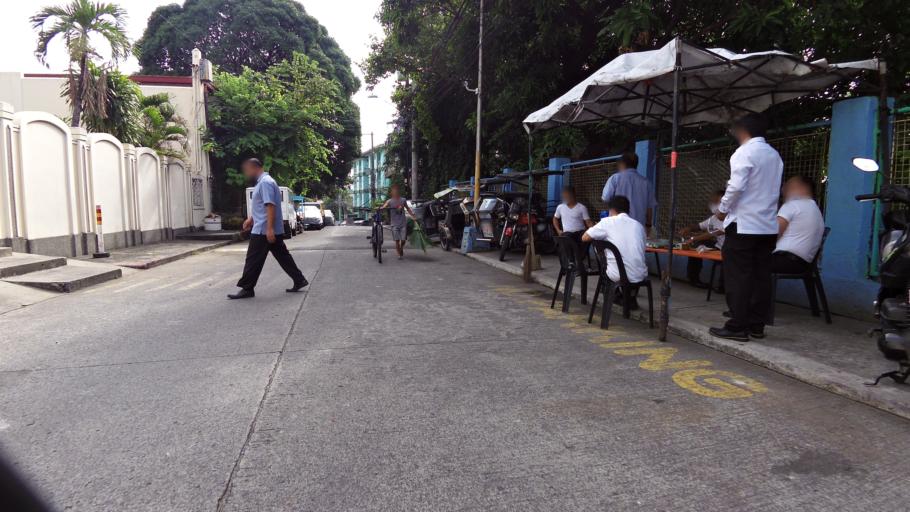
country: PH
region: Metro Manila
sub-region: Pasig
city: Pasig City
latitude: 14.5667
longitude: 121.0594
